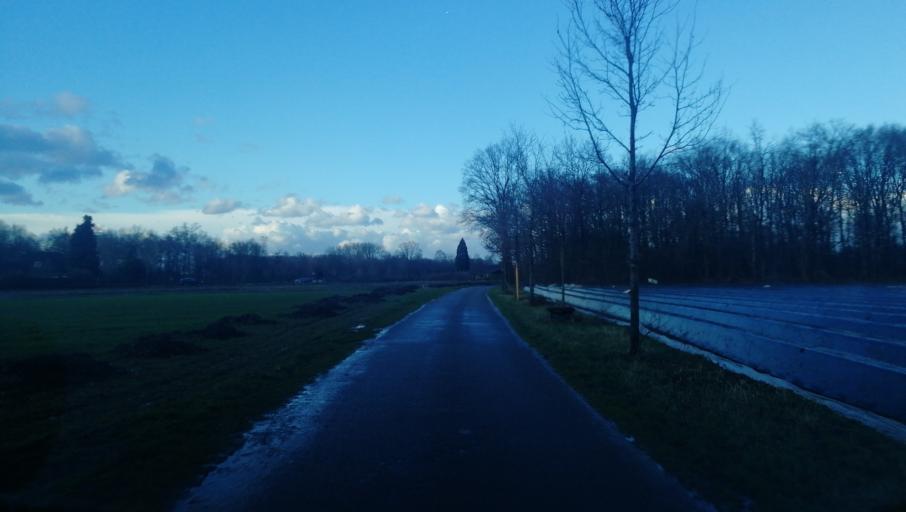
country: NL
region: Limburg
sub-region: Gemeente Peel en Maas
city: Maasbree
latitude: 51.3425
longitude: 6.0332
